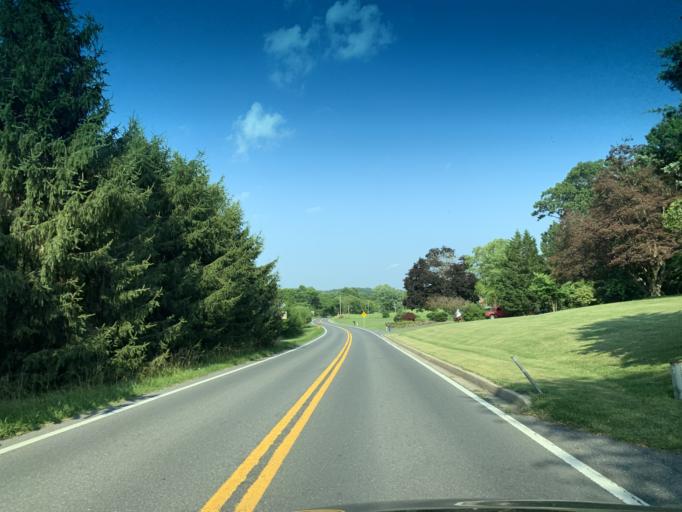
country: US
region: Maryland
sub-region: Frederick County
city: Green Valley
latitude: 39.2770
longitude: -77.3331
